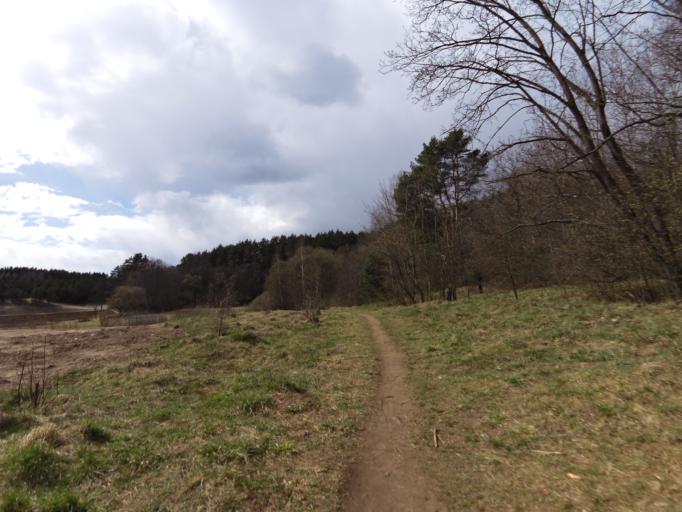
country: LT
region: Vilnius County
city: Pilaite
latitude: 54.6995
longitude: 25.1895
